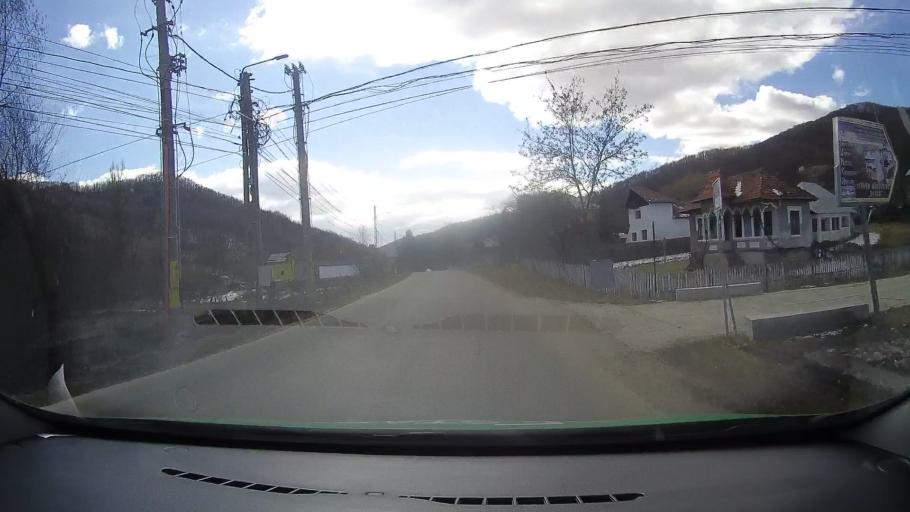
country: RO
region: Dambovita
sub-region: Comuna Vulcana Bai
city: Vulcana Bai
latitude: 45.0660
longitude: 25.3780
